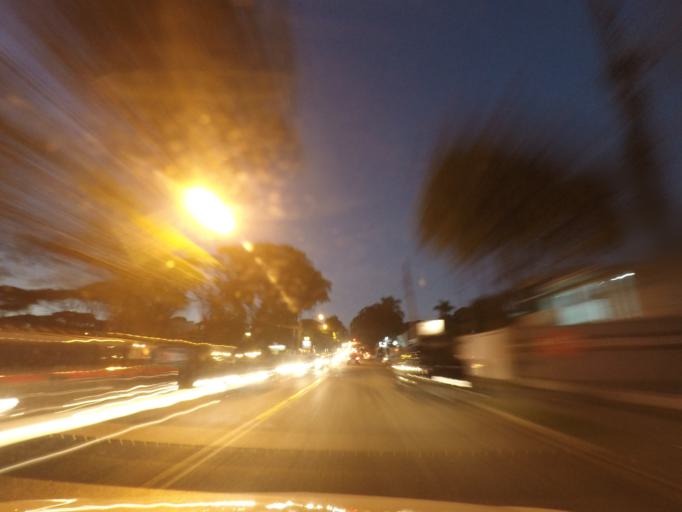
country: BR
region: Parana
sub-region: Curitiba
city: Curitiba
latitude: -25.4585
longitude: -49.2790
